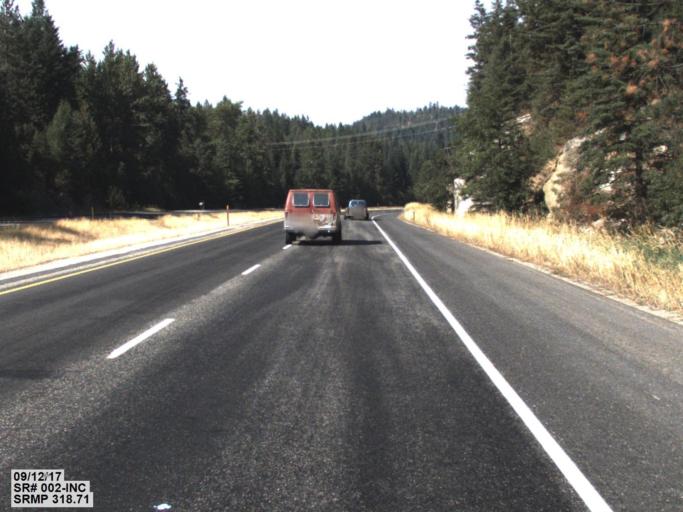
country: US
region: Washington
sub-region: Spokane County
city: Deer Park
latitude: 48.0880
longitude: -117.3258
